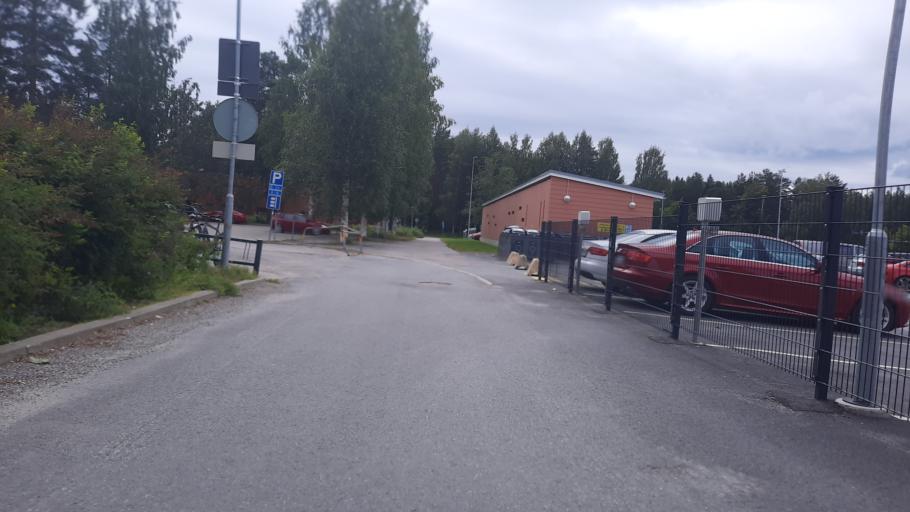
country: FI
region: North Karelia
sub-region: Joensuu
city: Joensuu
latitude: 62.6144
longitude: 29.8162
